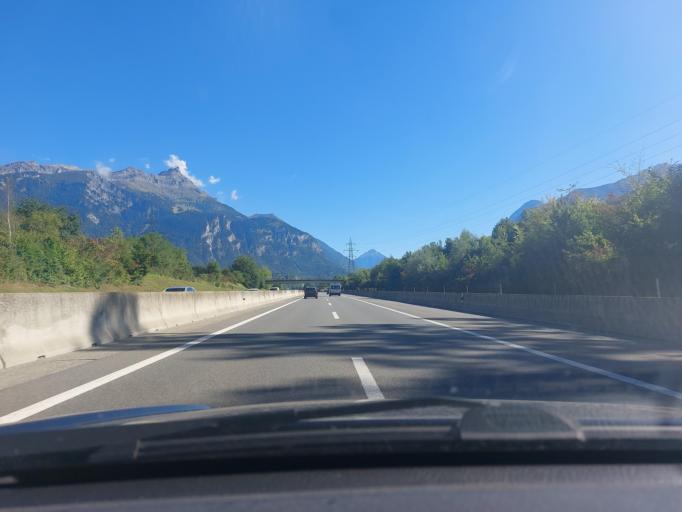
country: CH
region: Valais
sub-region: Monthey District
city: Monthey
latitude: 46.2633
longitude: 6.9785
